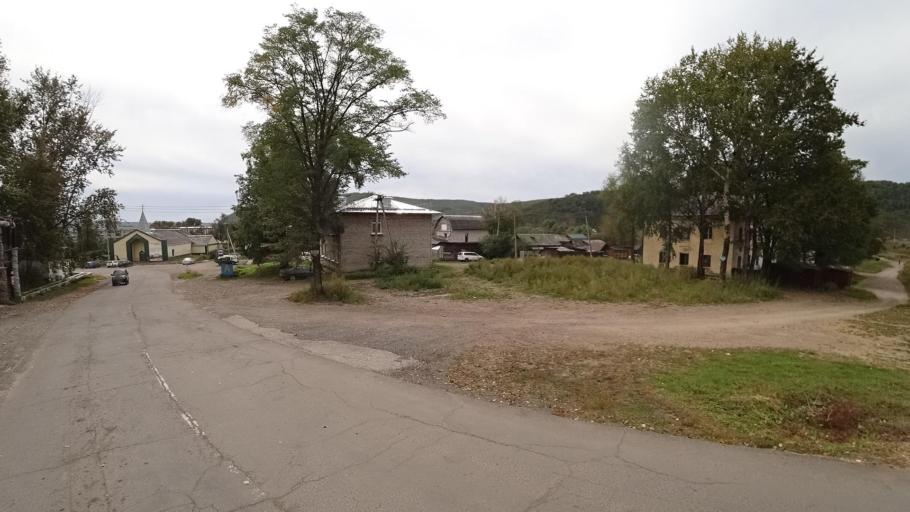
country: RU
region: Jewish Autonomous Oblast
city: Khingansk
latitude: 49.0166
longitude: 131.0547
